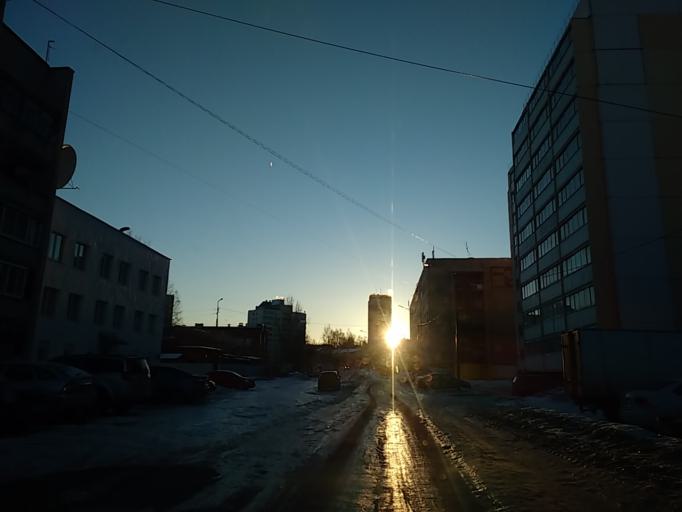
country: RU
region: Republic of Karelia
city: Petrozavodsk
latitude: 61.7763
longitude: 34.3843
